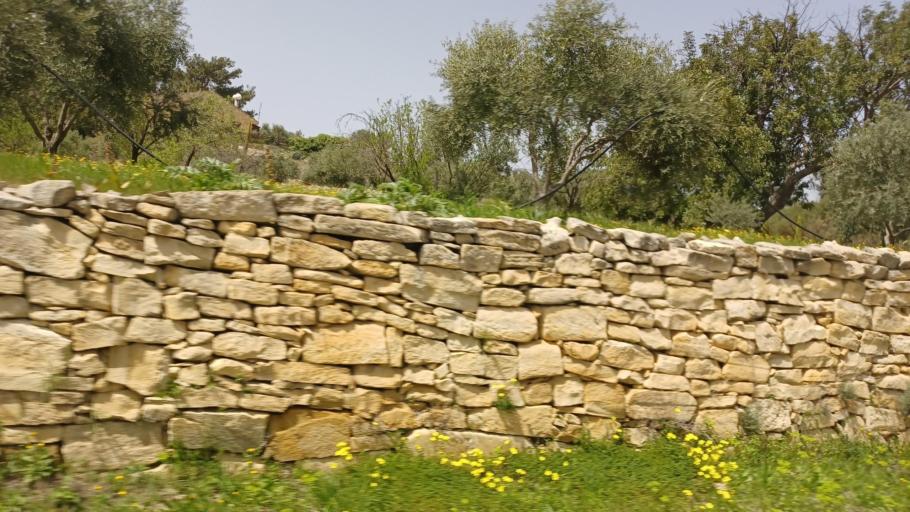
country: CY
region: Limassol
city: Pachna
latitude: 34.7506
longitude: 32.7456
